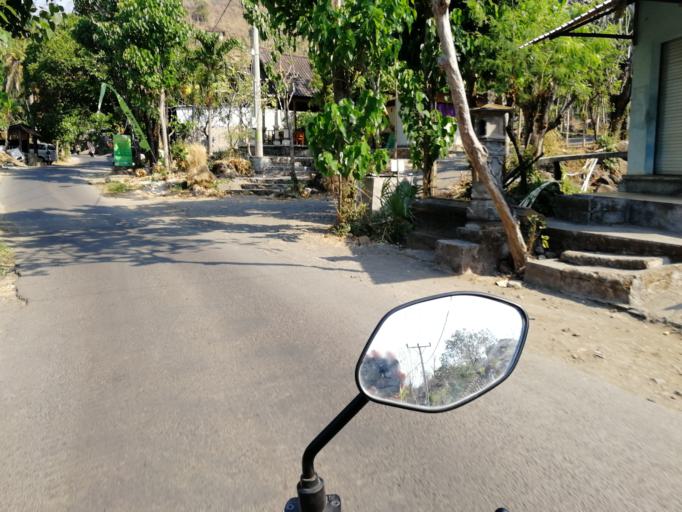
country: ID
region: Bali
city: Biaslantang Kaler
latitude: -8.3574
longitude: 115.6919
